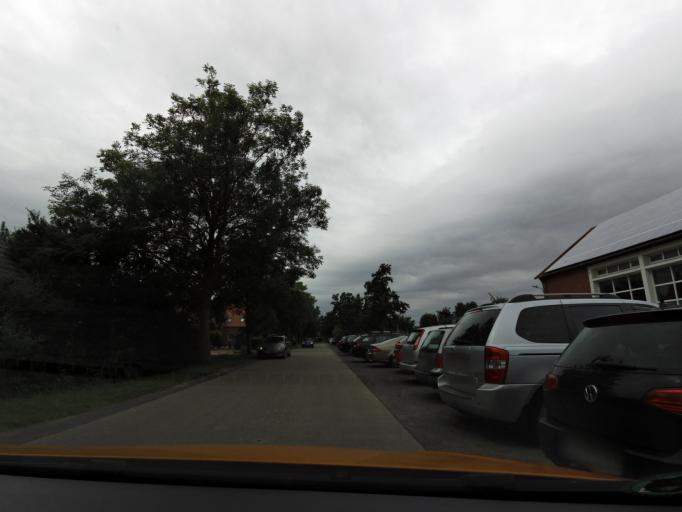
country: DE
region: Lower Saxony
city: Wirdum
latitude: 53.4992
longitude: 7.1004
